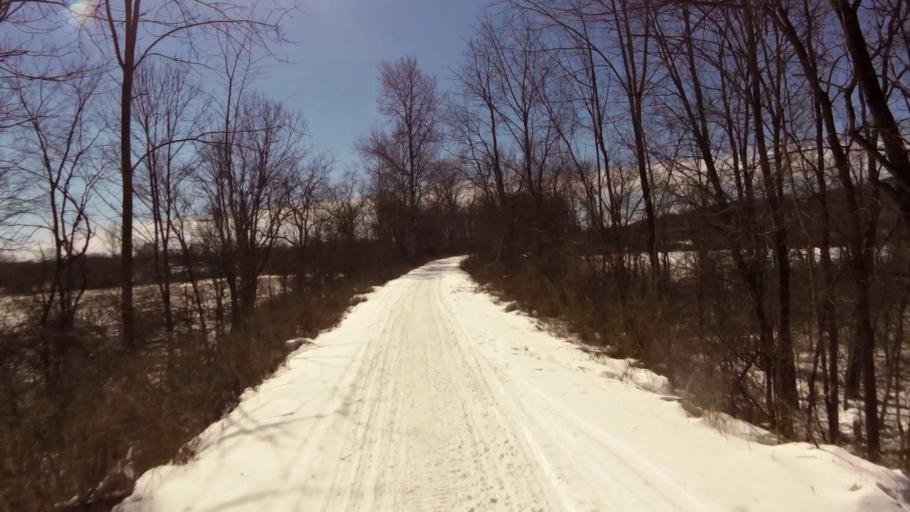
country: US
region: New York
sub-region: Allegany County
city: Houghton
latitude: 42.3531
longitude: -78.1255
